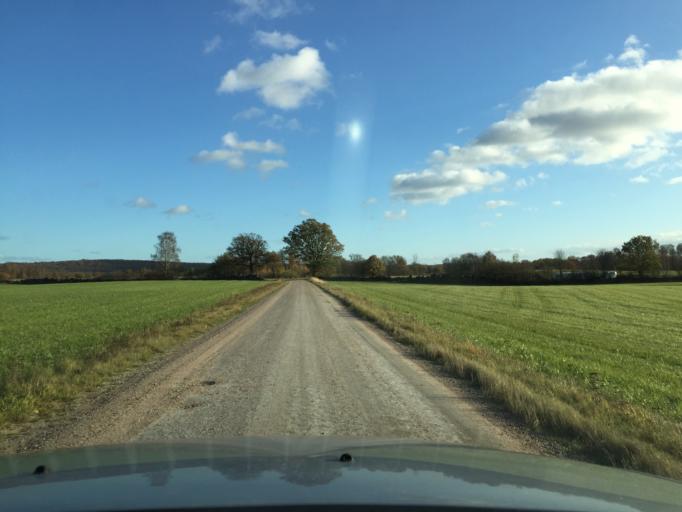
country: SE
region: Skane
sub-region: Hassleholms Kommun
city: Tormestorp
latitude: 56.0670
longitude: 13.7159
